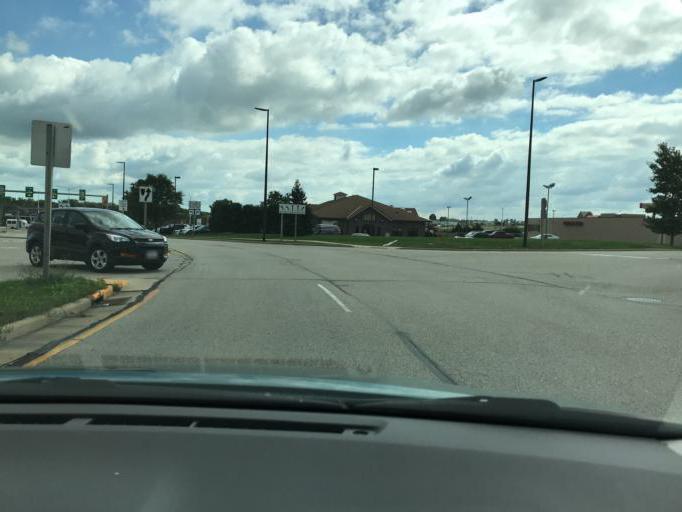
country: US
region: Wisconsin
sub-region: Kenosha County
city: Pleasant Prairie
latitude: 42.5691
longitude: -87.9504
